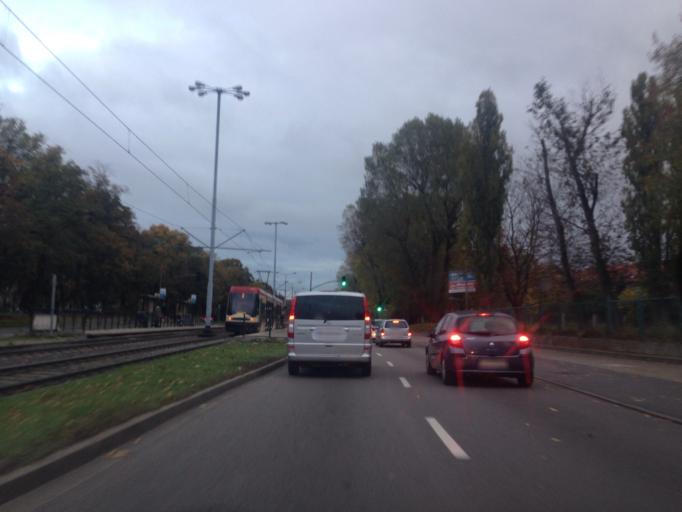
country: PL
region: Pomeranian Voivodeship
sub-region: Gdansk
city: Gdansk
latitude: 54.3796
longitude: 18.6221
